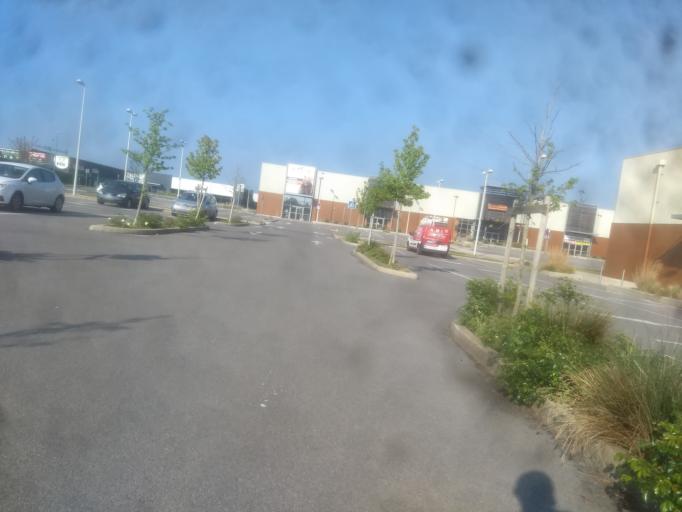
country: FR
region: Nord-Pas-de-Calais
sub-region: Departement du Pas-de-Calais
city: Beaurains
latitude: 50.2639
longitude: 2.7998
